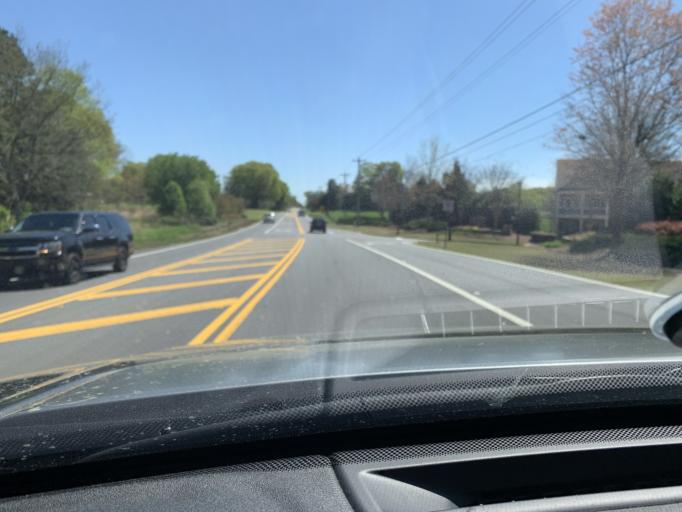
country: US
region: Georgia
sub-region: Forsyth County
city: Cumming
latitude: 34.2261
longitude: -84.2270
